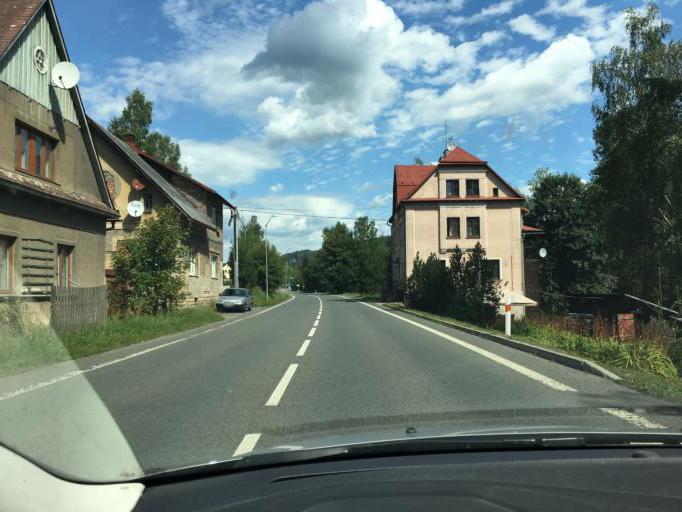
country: CZ
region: Liberecky
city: Velke Hamry
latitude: 50.7096
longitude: 15.3163
